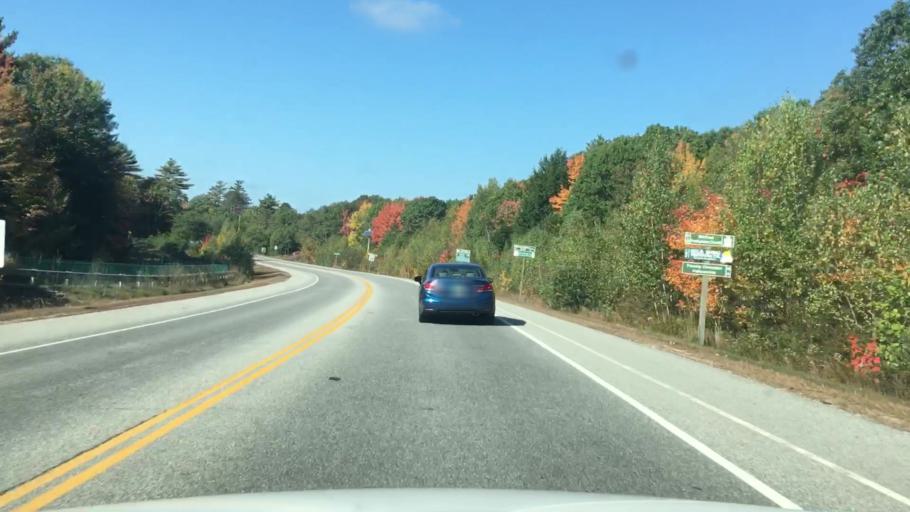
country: US
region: Maine
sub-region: Sagadahoc County
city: Topsham
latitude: 43.9371
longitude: -69.9606
